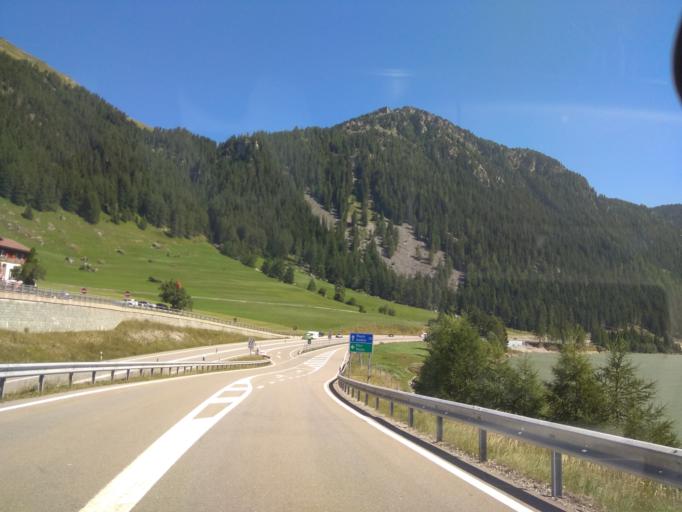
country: CH
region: Grisons
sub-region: Hinterrhein District
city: Thusis
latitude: 46.5691
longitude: 9.3684
